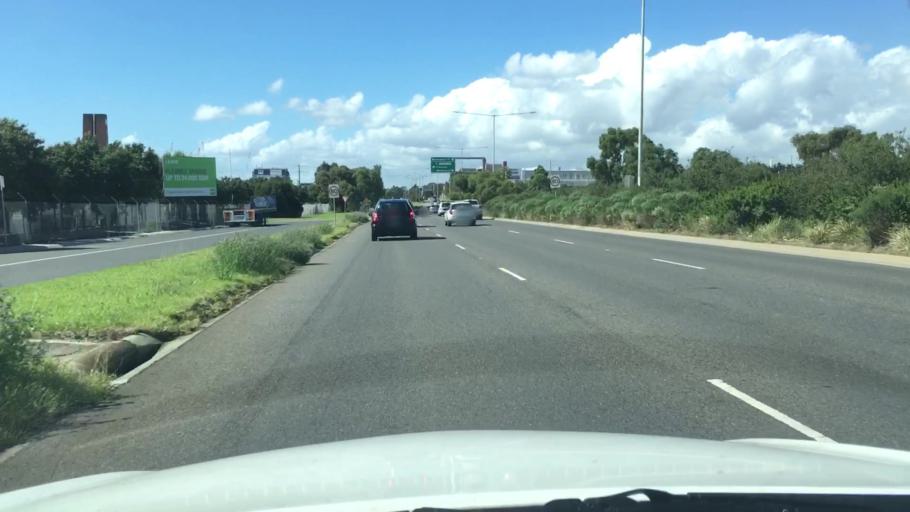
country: AU
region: Victoria
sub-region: Greater Dandenong
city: Springvale
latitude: -37.9341
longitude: 145.1411
